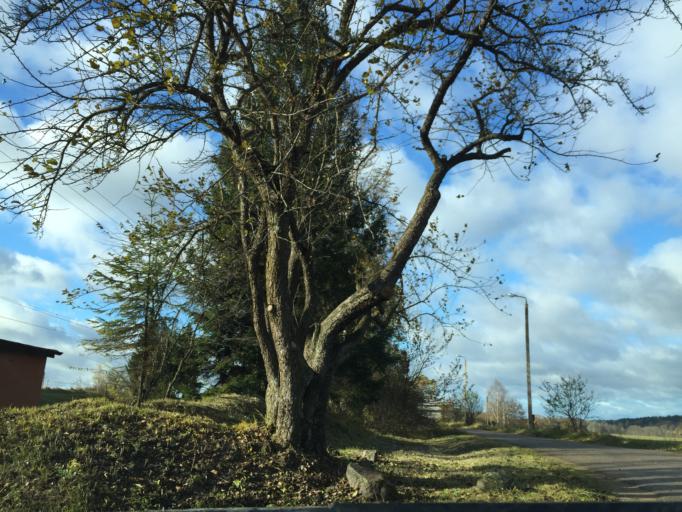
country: LV
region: Tukuma Rajons
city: Tukums
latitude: 56.9704
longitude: 23.2326
